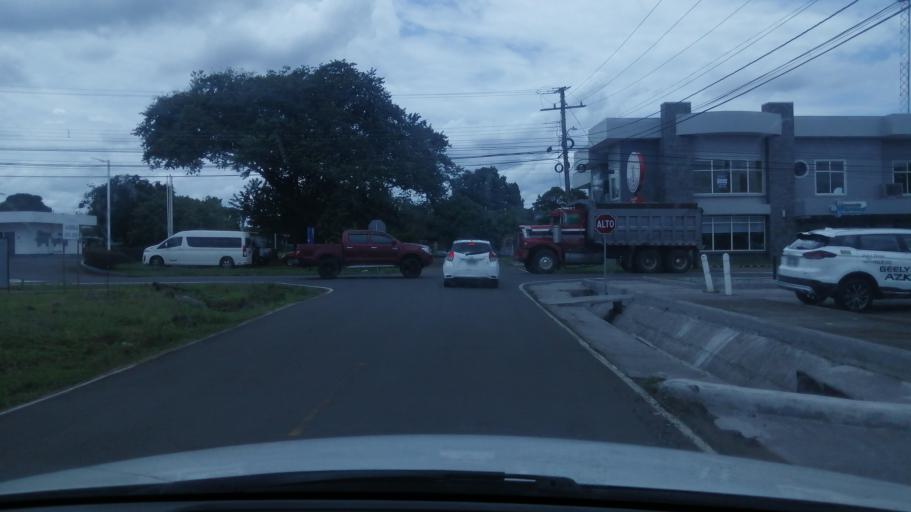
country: PA
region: Chiriqui
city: Mata del Nance
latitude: 8.4490
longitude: -82.4219
